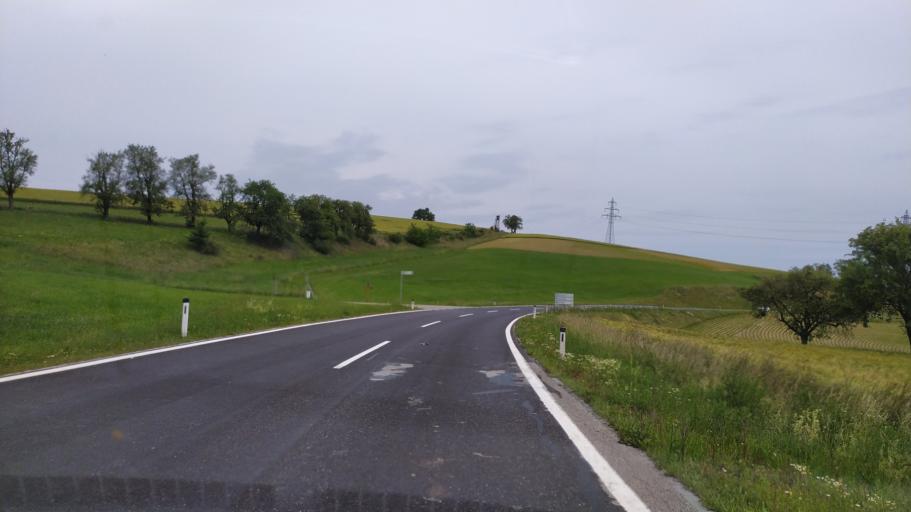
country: AT
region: Lower Austria
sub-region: Politischer Bezirk Amstetten
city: Strengberg
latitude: 48.1381
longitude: 14.6129
